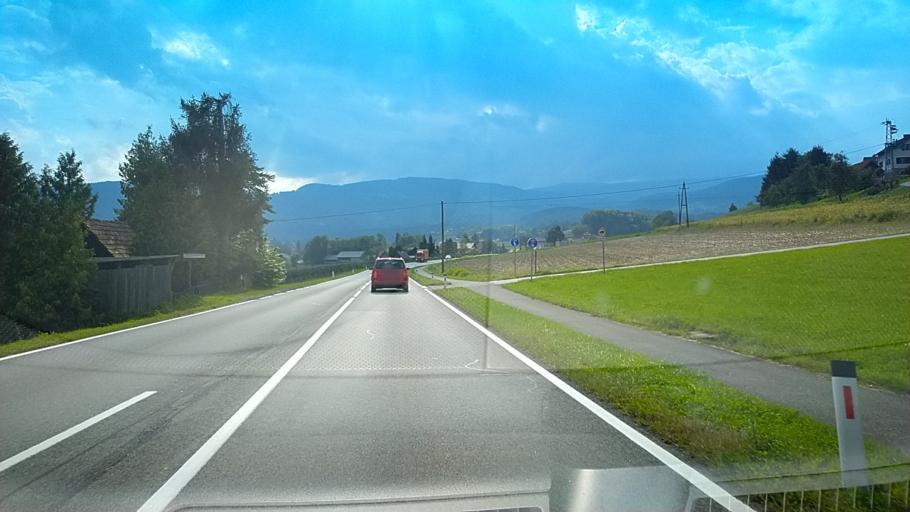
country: AT
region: Styria
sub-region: Politischer Bezirk Deutschlandsberg
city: Hollenegg
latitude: 46.7773
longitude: 15.2315
